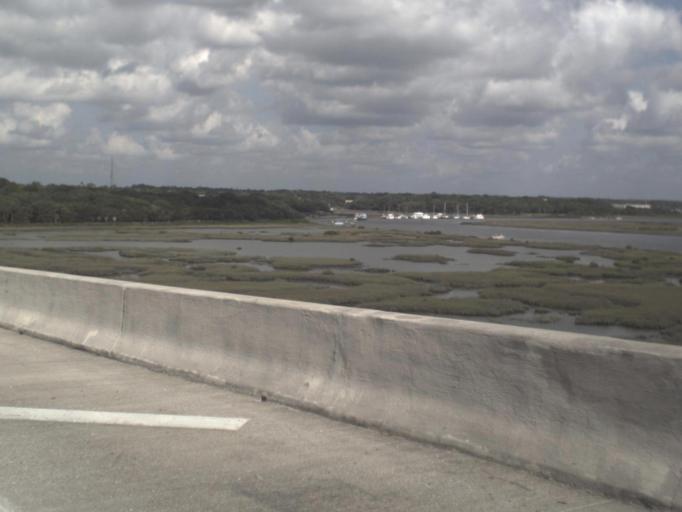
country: US
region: Florida
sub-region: Saint Johns County
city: Saint Augustine South
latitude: 29.8672
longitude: -81.3095
